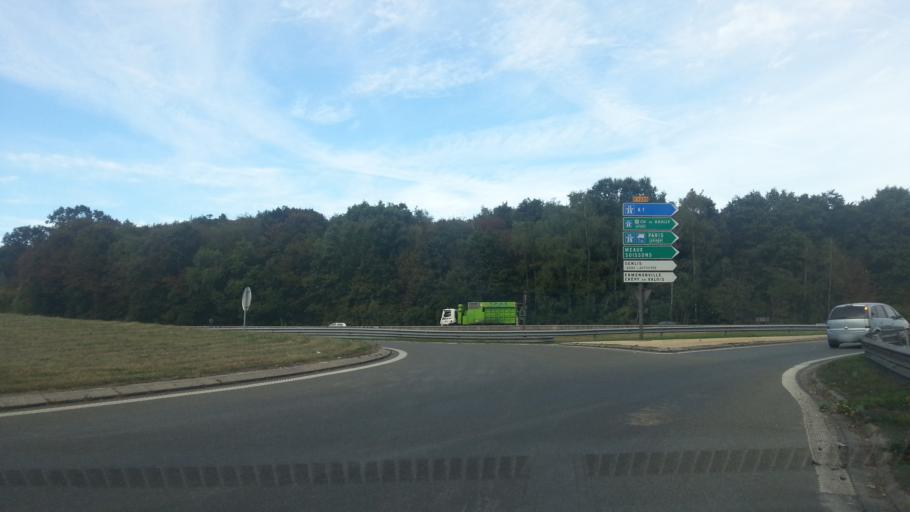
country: FR
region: Picardie
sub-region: Departement de l'Oise
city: Avilly-Saint-Leonard
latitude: 49.2165
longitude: 2.5561
